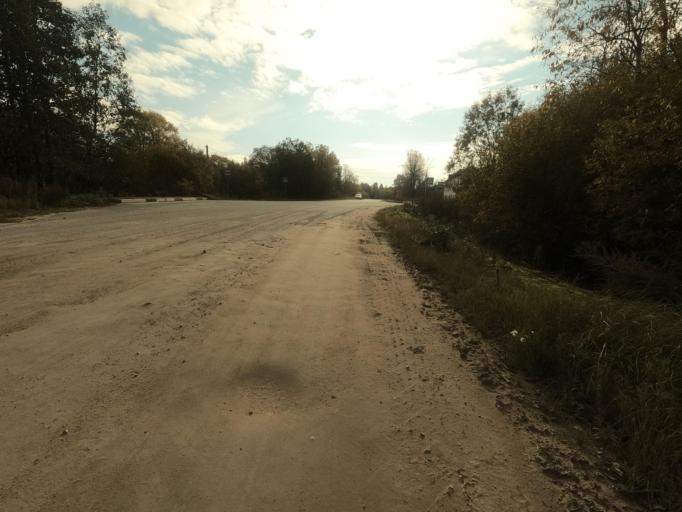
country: RU
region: Novgorod
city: Batetskiy
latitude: 58.8003
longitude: 30.6540
